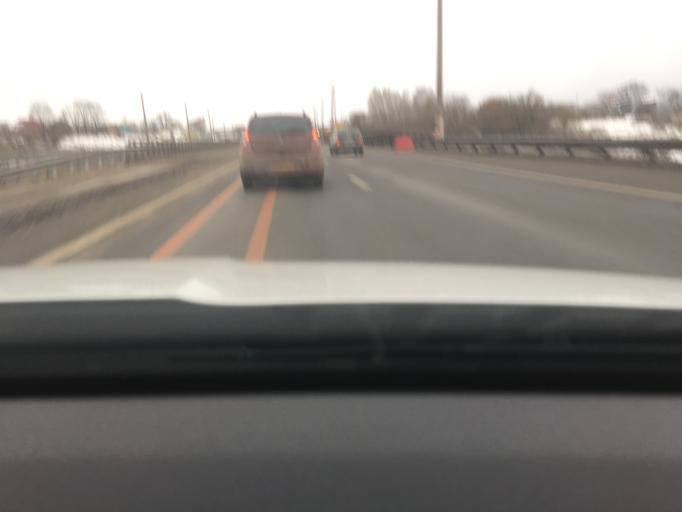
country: RU
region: Moskovskaya
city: Serpukhov
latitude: 54.8576
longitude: 37.4820
